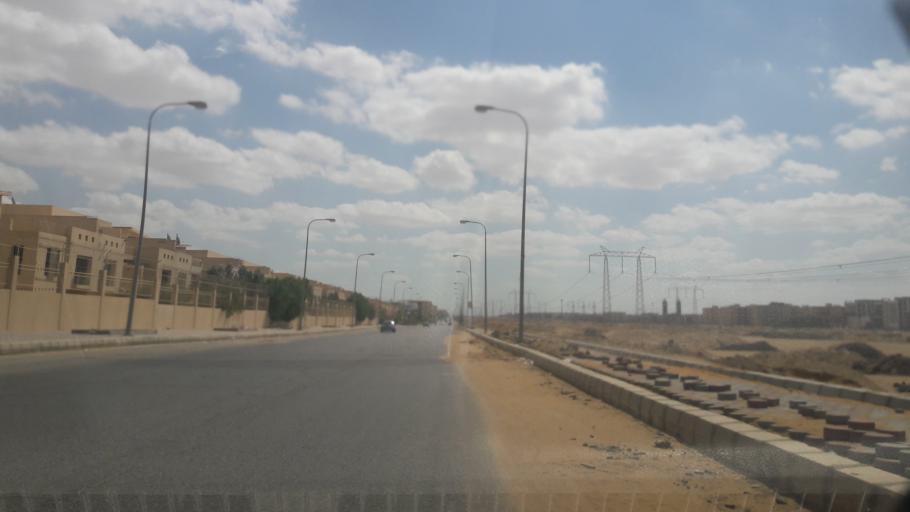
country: EG
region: Al Jizah
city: Madinat Sittah Uktubar
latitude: 29.9407
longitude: 31.0590
